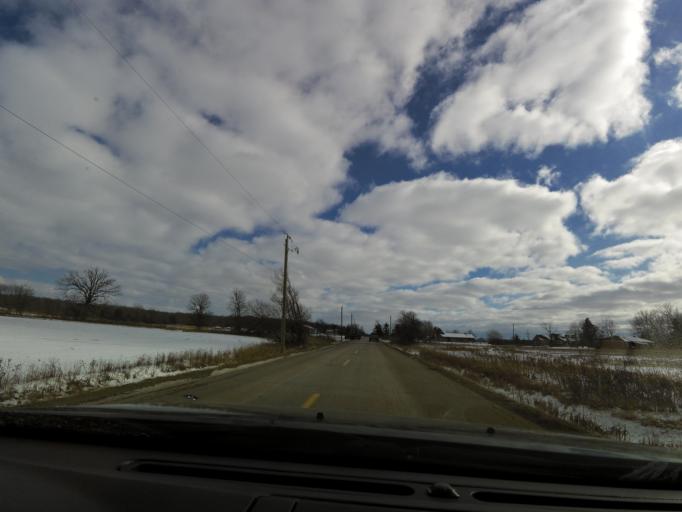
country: CA
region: Ontario
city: Hamilton
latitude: 43.1114
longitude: -79.6410
